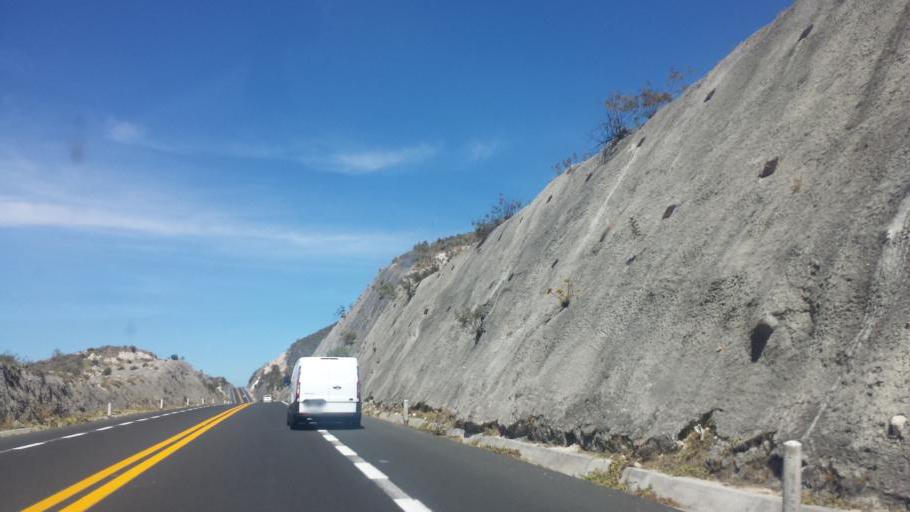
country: MX
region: Puebla
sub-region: San Jose Miahuatlan
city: San Pedro Tetitlan
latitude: 18.0000
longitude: -97.3550
